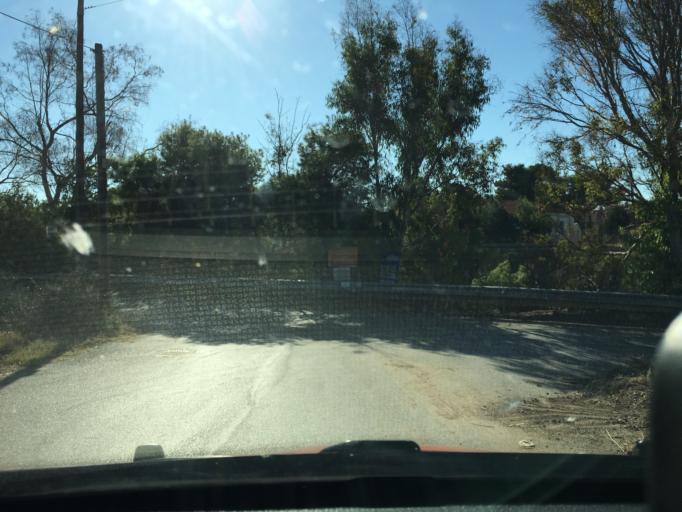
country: GR
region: Central Macedonia
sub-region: Nomos Chalkidikis
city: Nea Poteidaia
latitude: 40.1974
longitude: 23.3262
